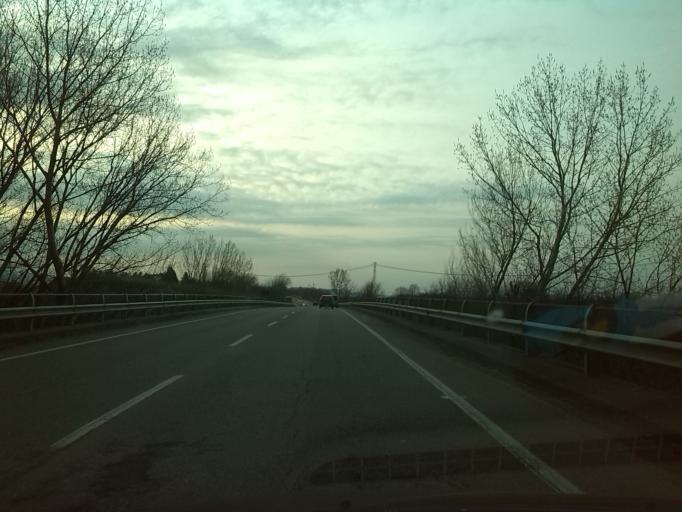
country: IT
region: Friuli Venezia Giulia
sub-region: Provincia di Udine
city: Cividale del Friuli
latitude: 46.0798
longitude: 13.4115
